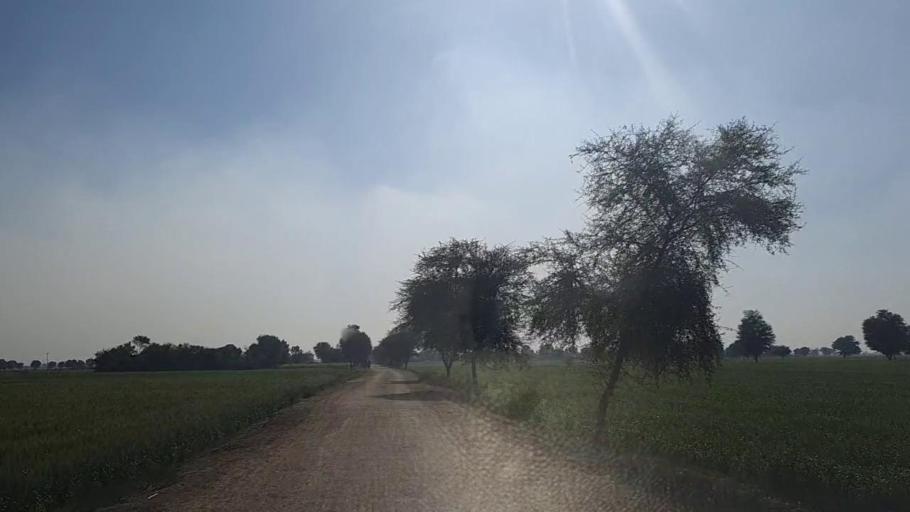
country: PK
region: Sindh
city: Shahpur Chakar
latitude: 26.2001
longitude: 68.6136
